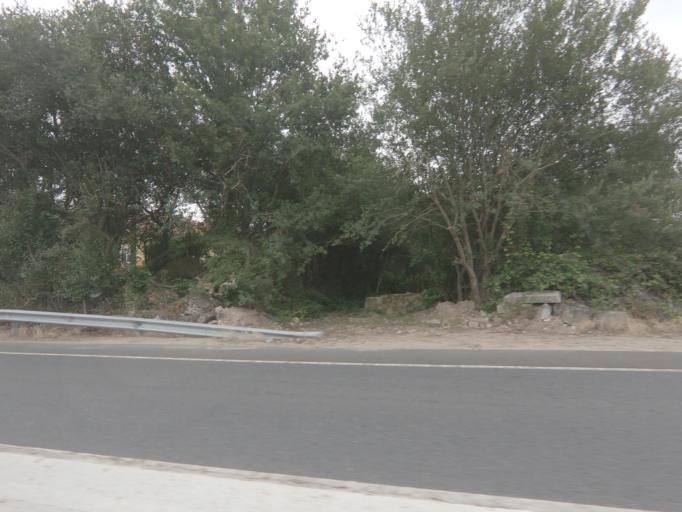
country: ES
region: Galicia
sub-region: Provincia de Pontevedra
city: Tomino
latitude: 41.9681
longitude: -8.7585
